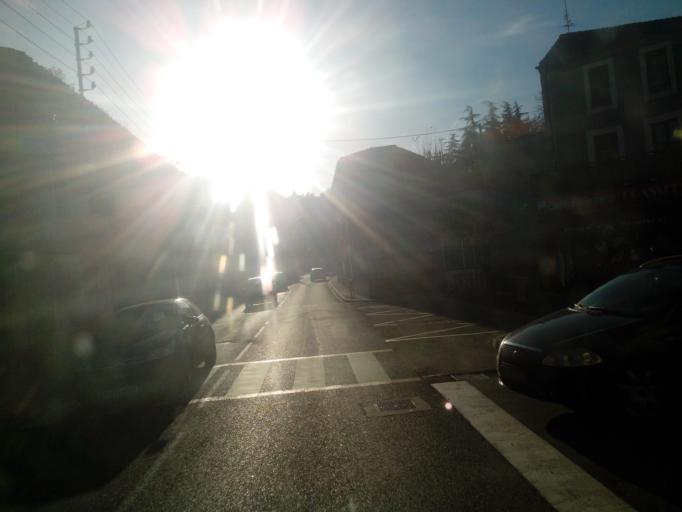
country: FR
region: Languedoc-Roussillon
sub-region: Departement de l'Aude
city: Couiza
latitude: 42.9413
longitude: 2.2536
